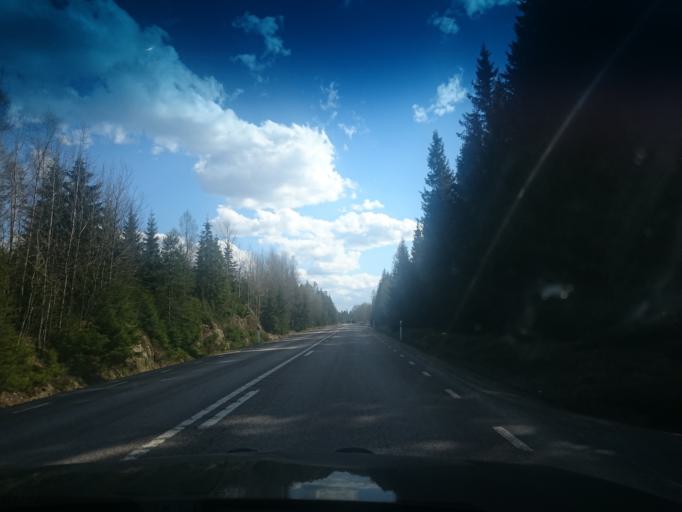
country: SE
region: Joenkoeping
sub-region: Vetlanda Kommun
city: Vetlanda
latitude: 57.2667
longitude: 15.1283
